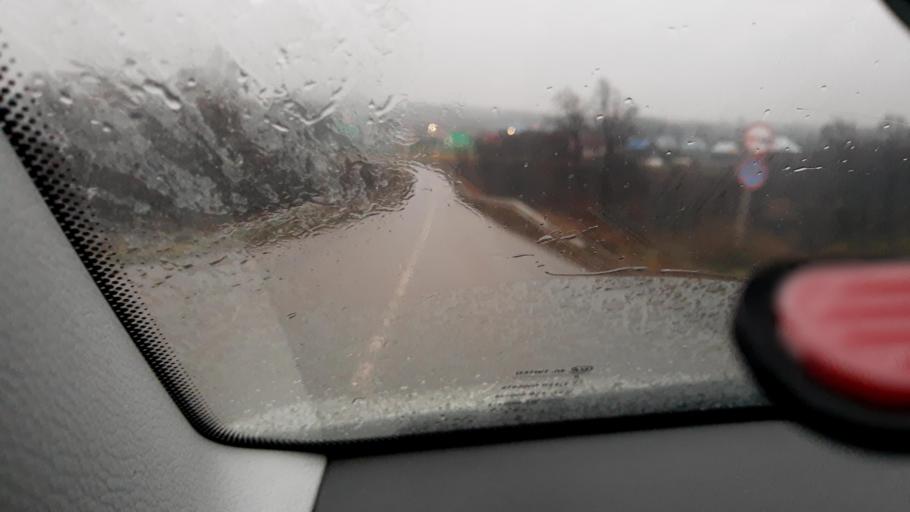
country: RU
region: Bashkortostan
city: Iglino
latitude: 54.9004
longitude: 56.2105
